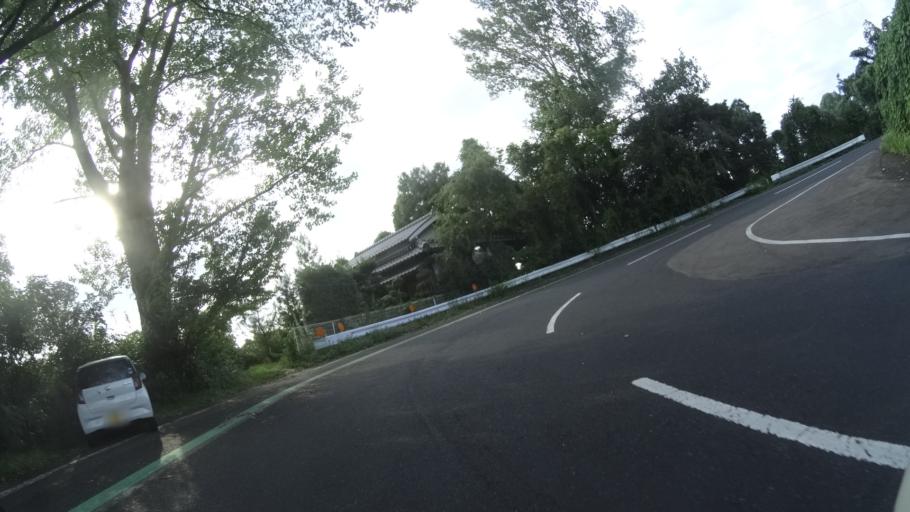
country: JP
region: Tottori
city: Kurayoshi
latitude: 35.4818
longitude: 133.8957
